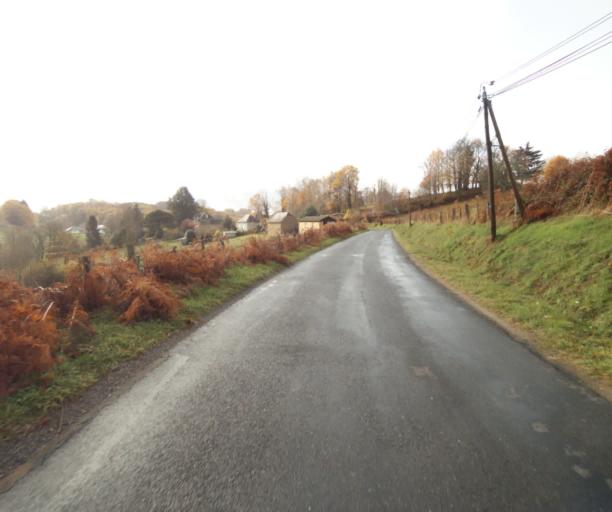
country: FR
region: Limousin
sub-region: Departement de la Correze
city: Cornil
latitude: 45.2165
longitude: 1.6425
